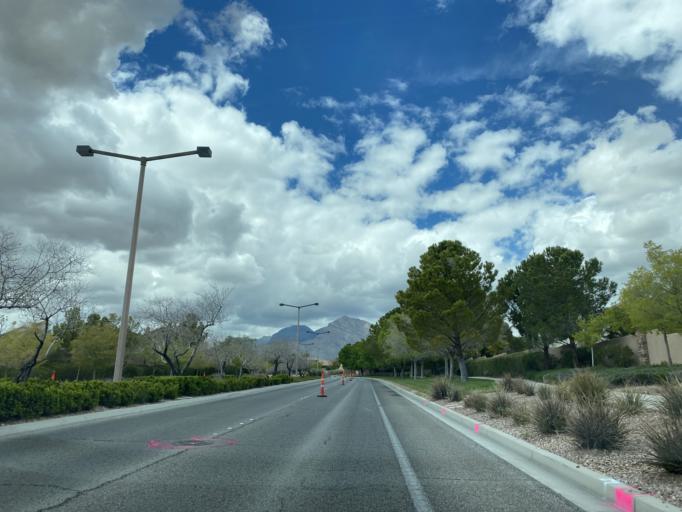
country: US
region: Nevada
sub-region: Clark County
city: Summerlin South
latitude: 36.1721
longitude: -115.3457
